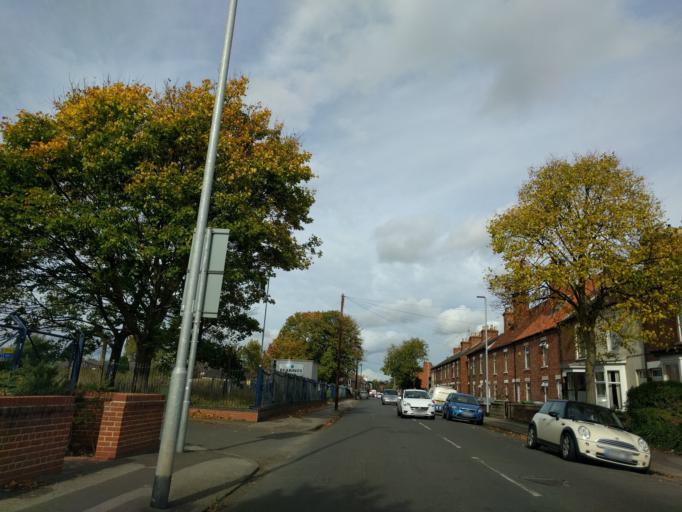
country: GB
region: England
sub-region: Nottinghamshire
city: Newark on Trent
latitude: 53.0688
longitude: -0.8052
